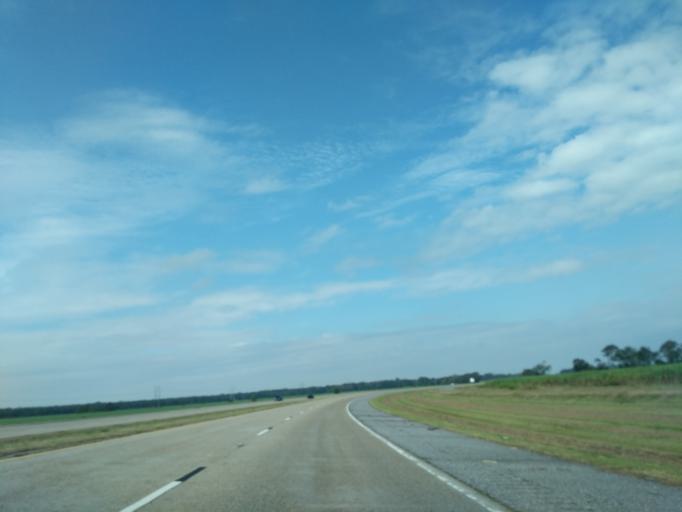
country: US
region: Louisiana
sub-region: Saint Mary Parish
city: Franklin
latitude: 29.7577
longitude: -91.4705
